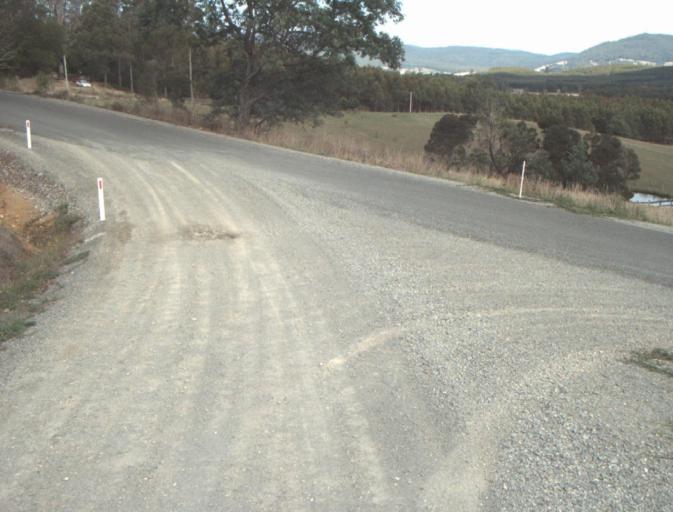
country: AU
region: Tasmania
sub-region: Launceston
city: Mayfield
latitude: -41.1921
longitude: 147.1805
